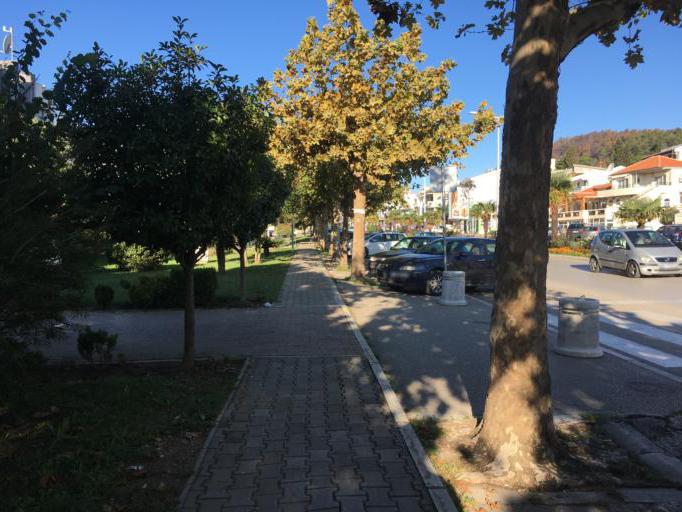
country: ME
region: Ulcinj
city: Ulcinj
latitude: 41.9294
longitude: 19.2179
